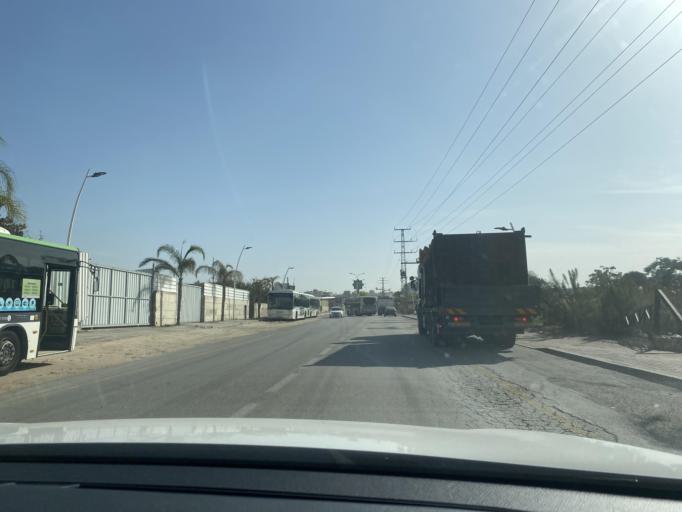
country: IL
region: Central District
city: Jaljulya
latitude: 32.1363
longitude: 34.9625
